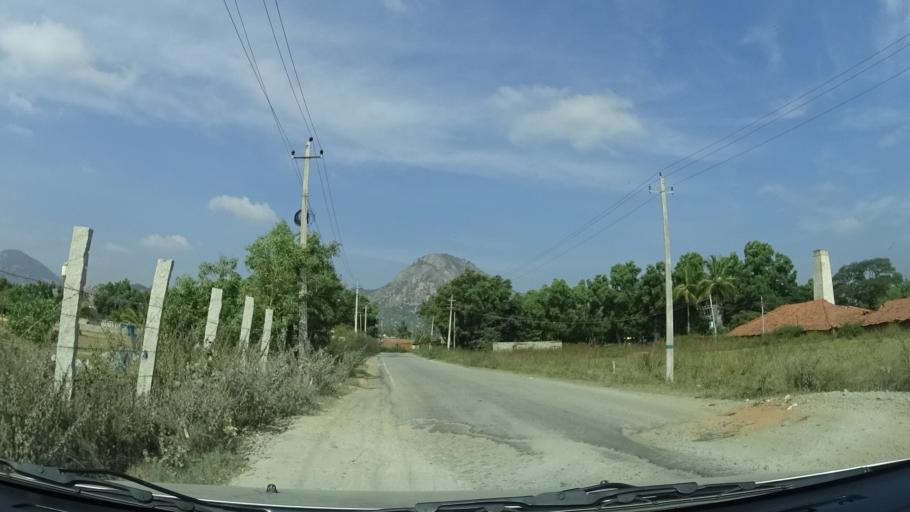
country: IN
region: Karnataka
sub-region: Chikkaballapur
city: Chik Ballapur
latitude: 13.4056
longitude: 77.7126
